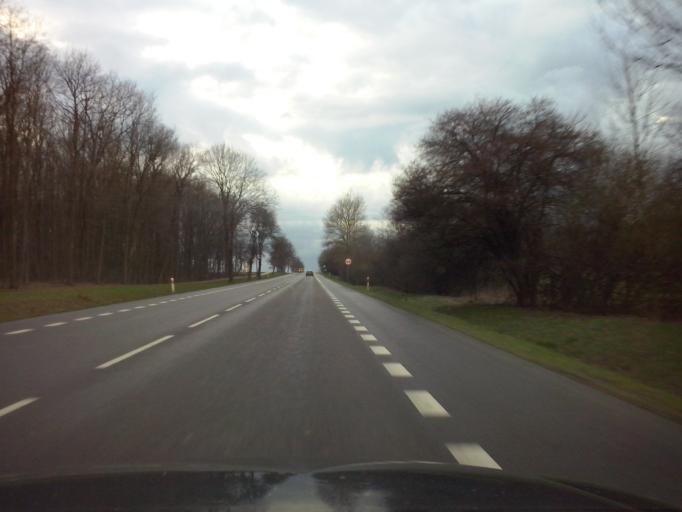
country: PL
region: Lublin Voivodeship
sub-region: Chelm
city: Chelm
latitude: 51.1571
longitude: 23.4046
